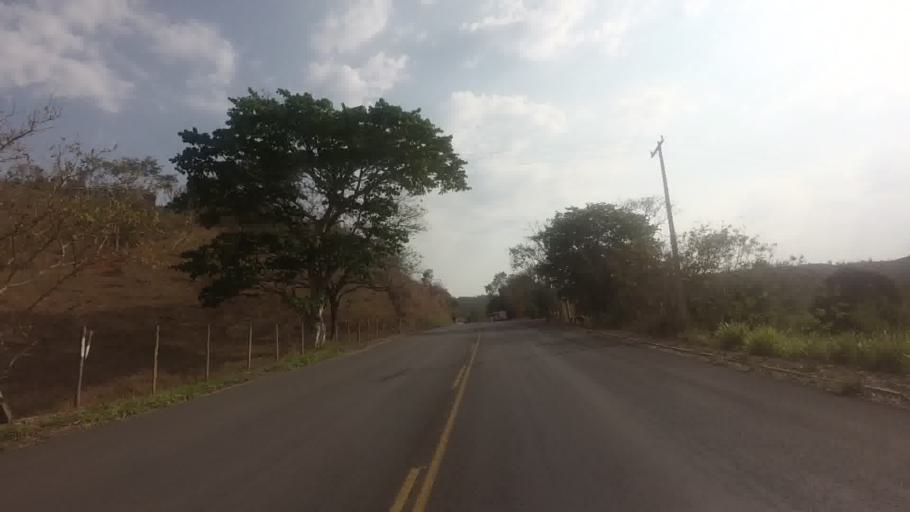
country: BR
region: Rio de Janeiro
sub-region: Itaperuna
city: Itaperuna
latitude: -21.3249
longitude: -41.8730
